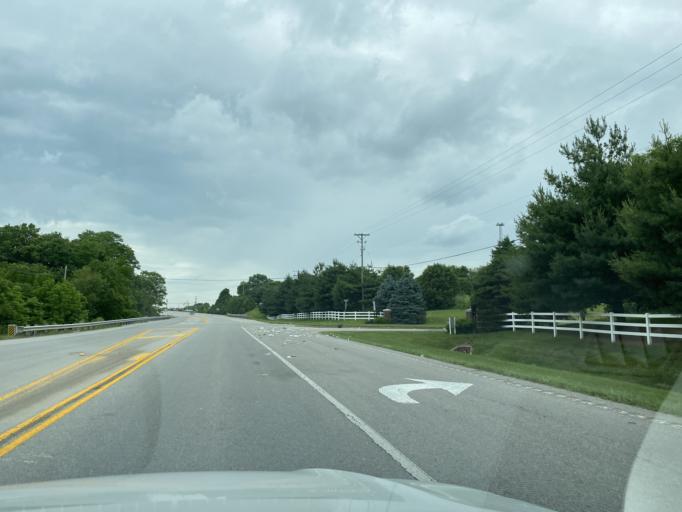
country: US
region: Kentucky
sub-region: Scott County
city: Georgetown
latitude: 38.2174
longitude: -84.5275
